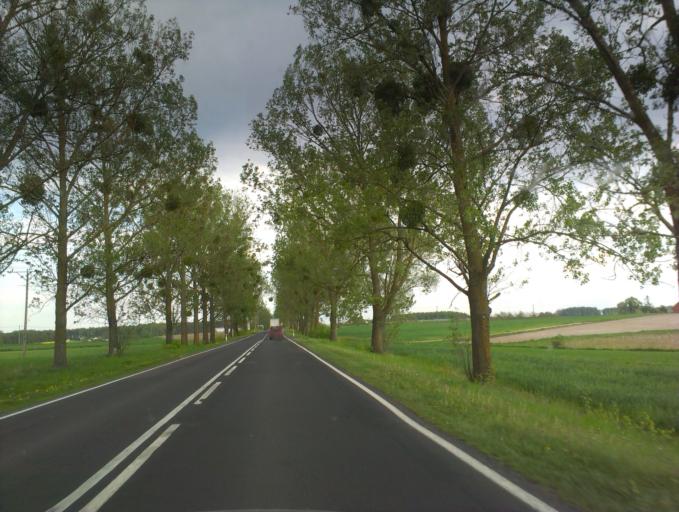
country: PL
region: Kujawsko-Pomorskie
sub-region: Powiat swiecki
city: Drzycim
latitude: 53.4268
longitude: 18.3234
